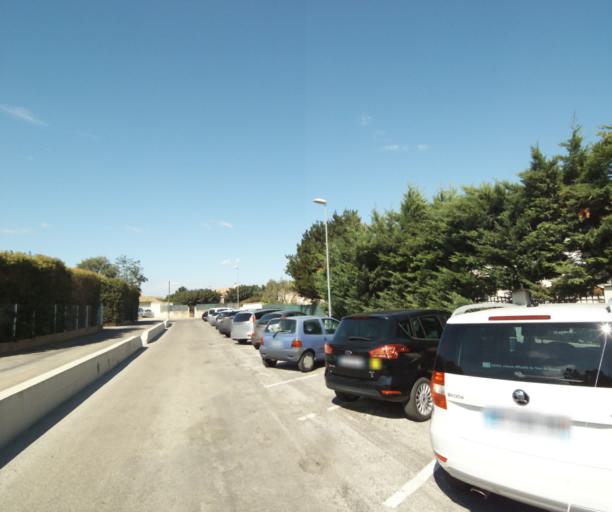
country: FR
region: Languedoc-Roussillon
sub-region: Departement du Gard
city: Bouillargues
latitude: 43.8007
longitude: 4.4353
